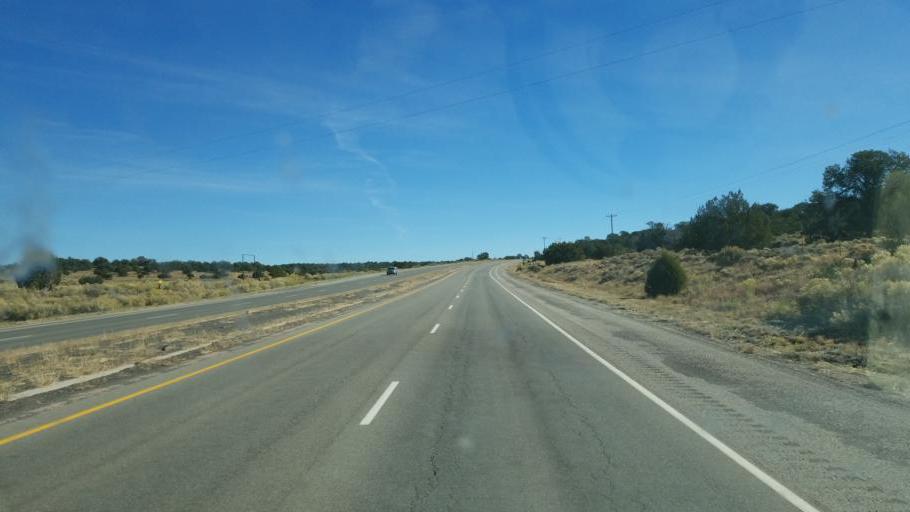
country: US
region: New Mexico
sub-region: McKinley County
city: Twin Lakes
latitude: 35.6349
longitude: -108.8861
